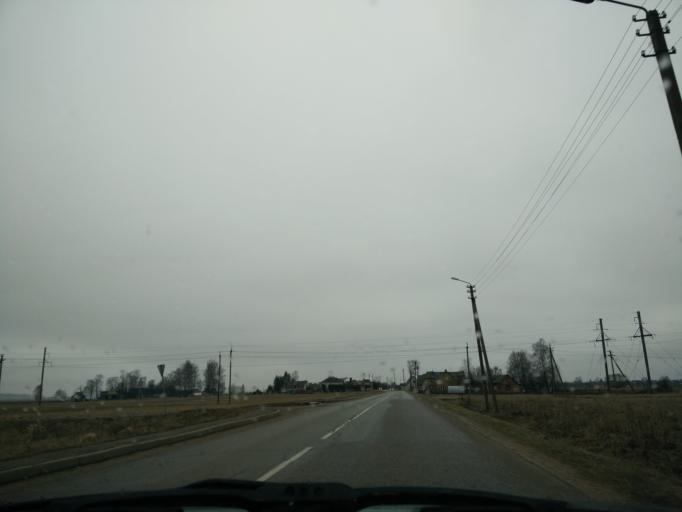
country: LT
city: Raseiniai
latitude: 55.3768
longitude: 23.1035
